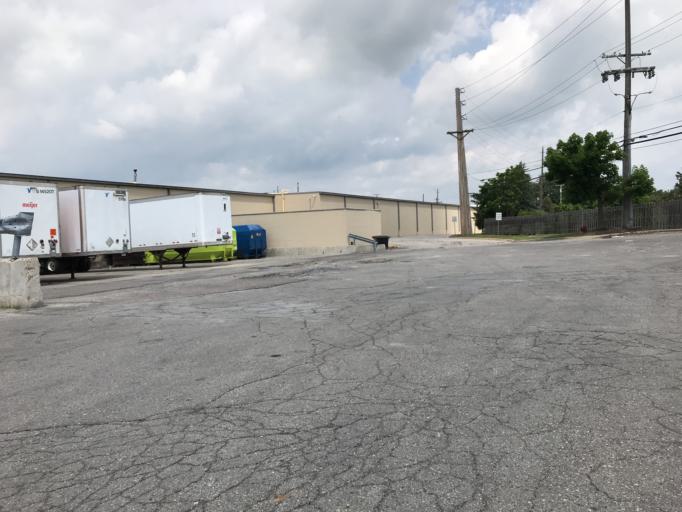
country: US
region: Michigan
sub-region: Oakland County
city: Bingham Farms
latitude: 42.4994
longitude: -83.2813
